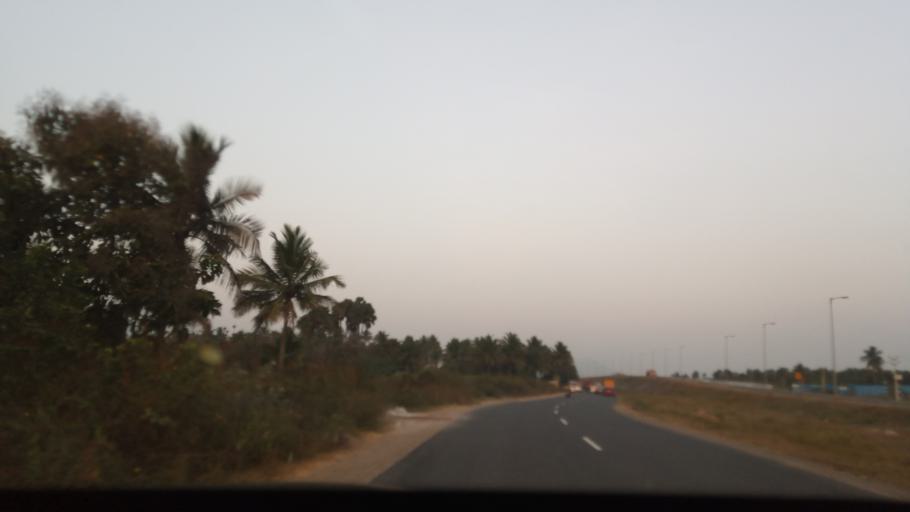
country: IN
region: Tamil Nadu
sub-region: Salem
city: Salem
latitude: 11.6615
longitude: 78.2251
